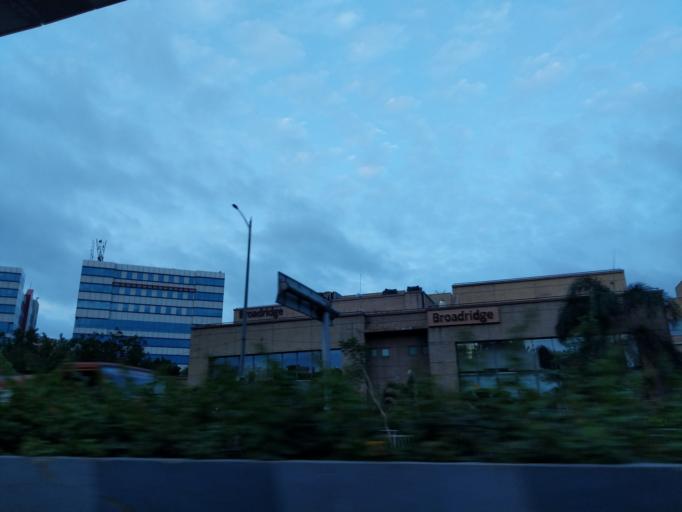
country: IN
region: Telangana
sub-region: Rangareddi
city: Kukatpalli
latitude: 17.4501
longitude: 78.3825
